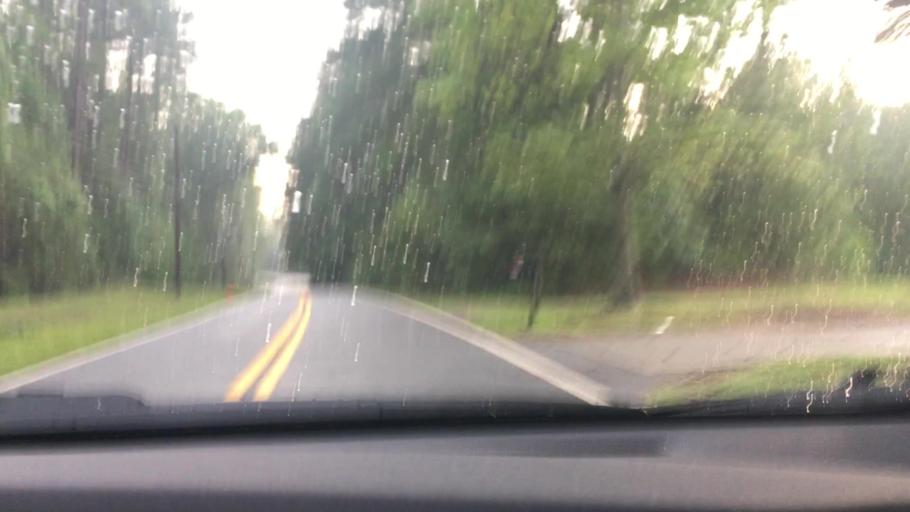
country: US
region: Georgia
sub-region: Fulton County
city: Union City
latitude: 33.6299
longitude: -84.5368
